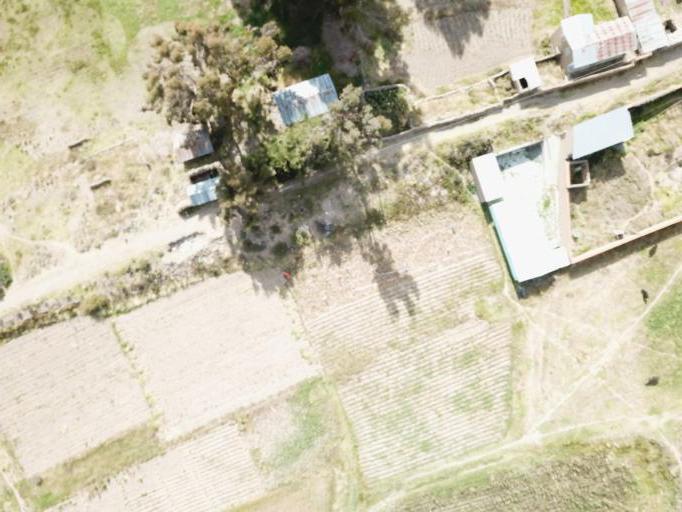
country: BO
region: La Paz
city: Achacachi
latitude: -16.0531
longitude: -68.8154
